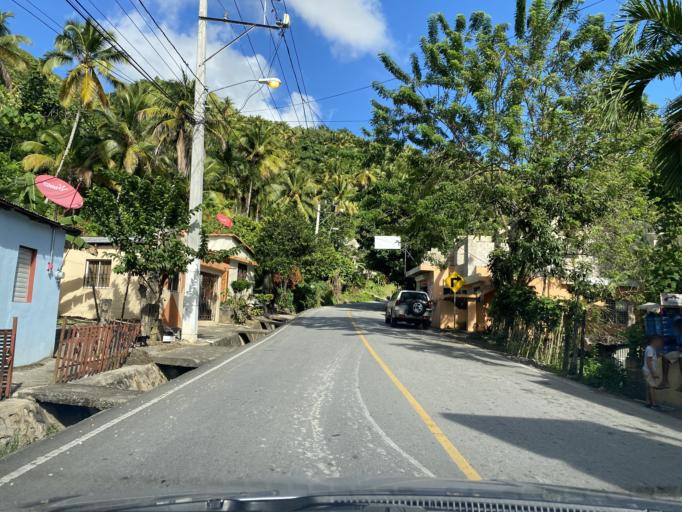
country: DO
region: Samana
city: Sanchez
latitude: 19.2336
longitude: -69.6039
